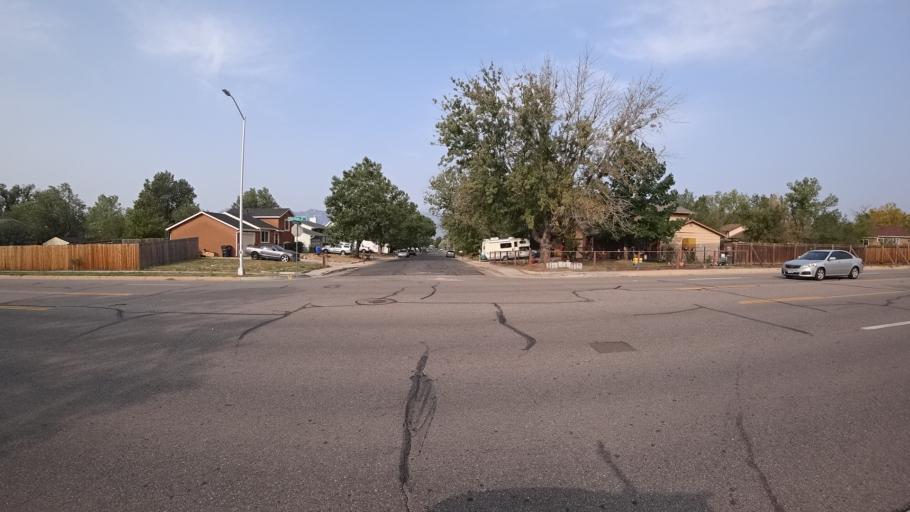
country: US
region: Colorado
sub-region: El Paso County
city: Stratmoor
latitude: 38.8010
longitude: -104.7432
